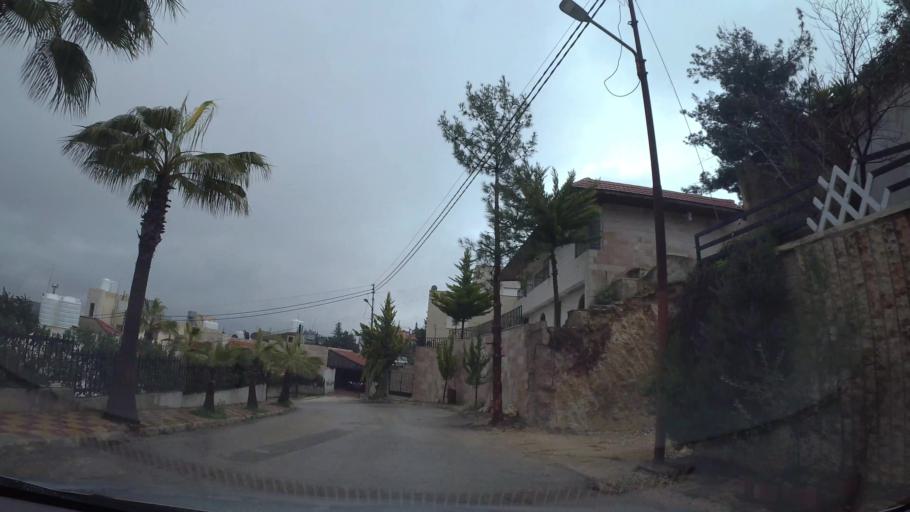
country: JO
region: Amman
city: Al Jubayhah
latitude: 32.0253
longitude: 35.8264
